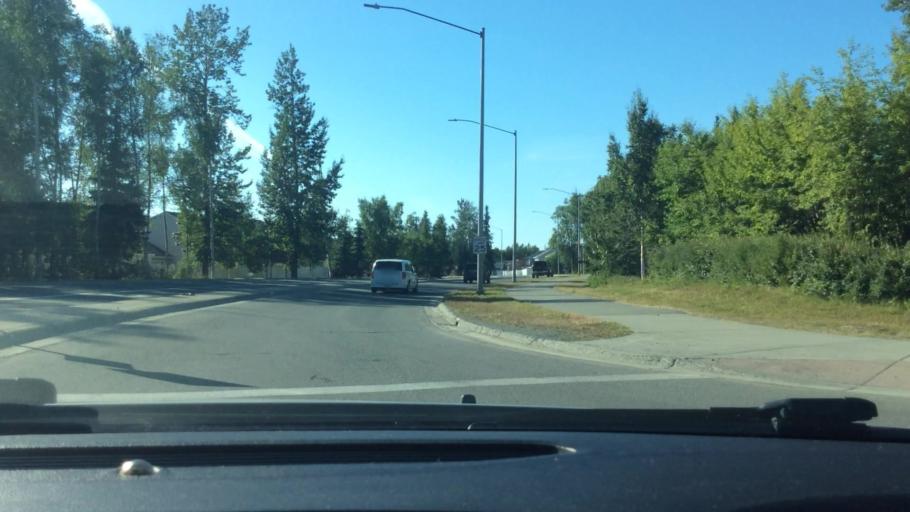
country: US
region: Alaska
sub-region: Anchorage Municipality
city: Anchorage
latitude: 61.2317
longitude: -149.7676
